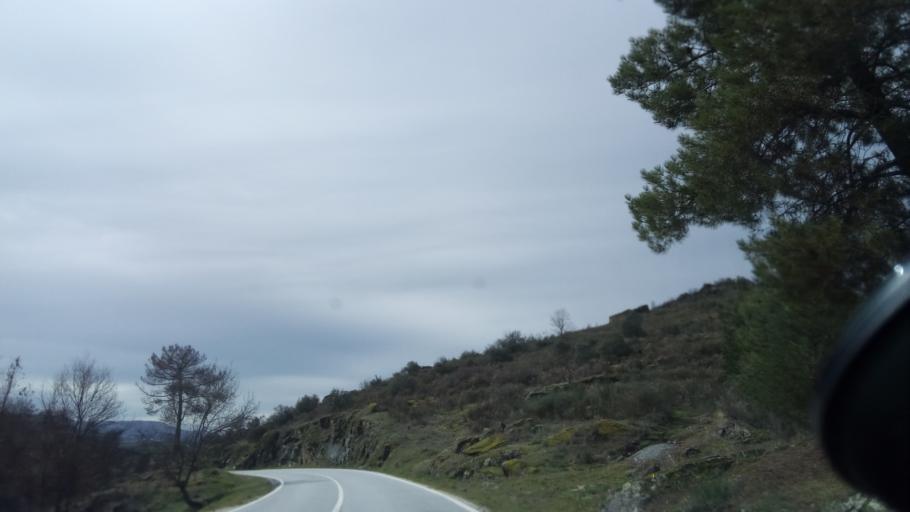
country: PT
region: Guarda
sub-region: Fornos de Algodres
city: Fornos de Algodres
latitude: 40.5677
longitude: -7.5558
